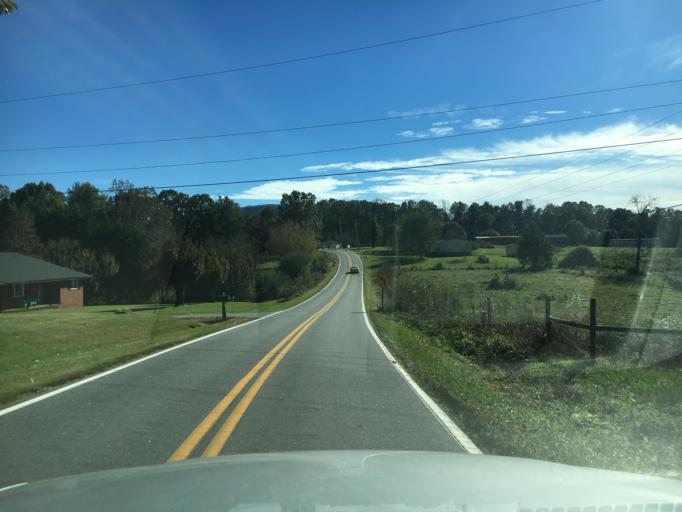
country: US
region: North Carolina
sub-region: Burke County
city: Salem
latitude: 35.6888
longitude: -81.7331
